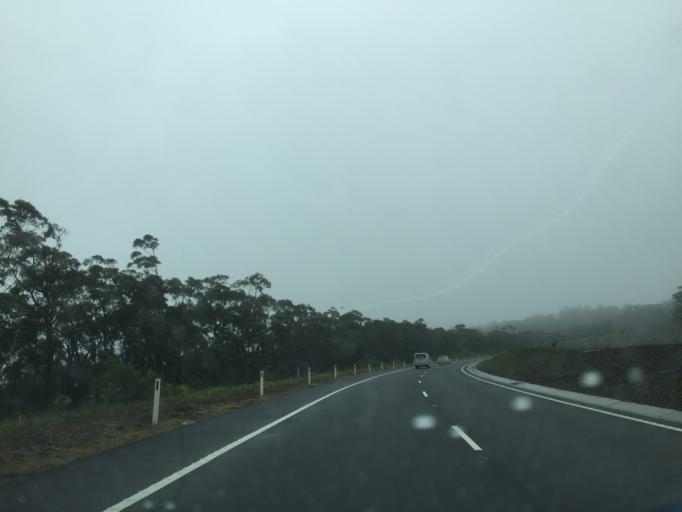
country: AU
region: New South Wales
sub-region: Blue Mountains Municipality
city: Lawson
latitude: -33.7277
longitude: 150.3930
